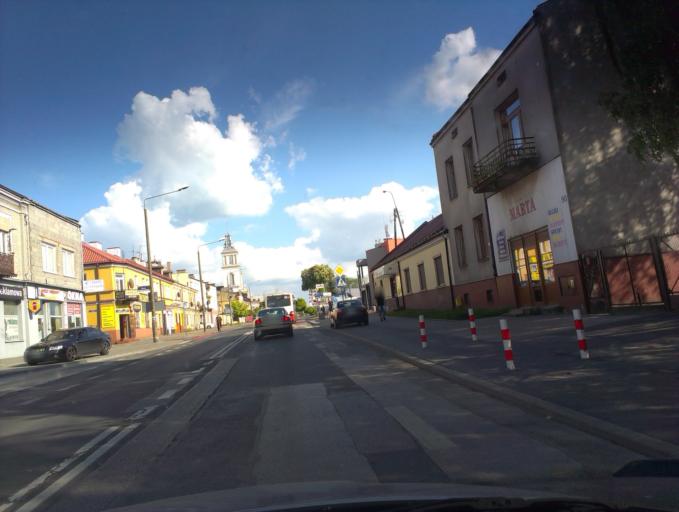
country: PL
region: Masovian Voivodeship
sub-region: Radom
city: Radom
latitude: 51.3895
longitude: 21.1720
